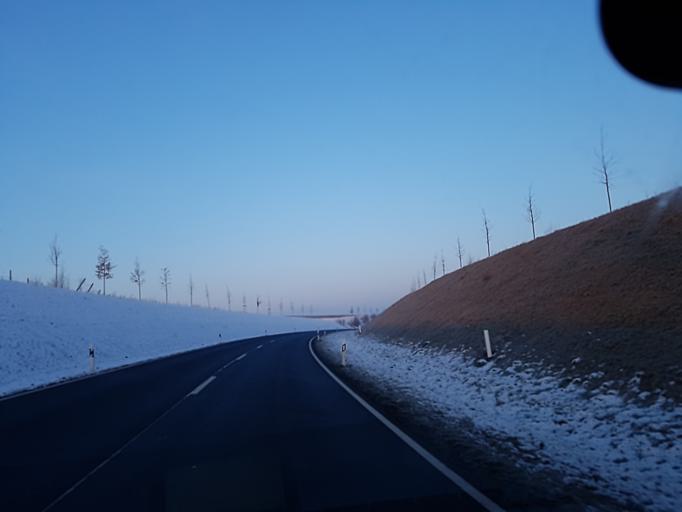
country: DE
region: Saxony
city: Mugeln
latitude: 51.2305
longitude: 13.0473
